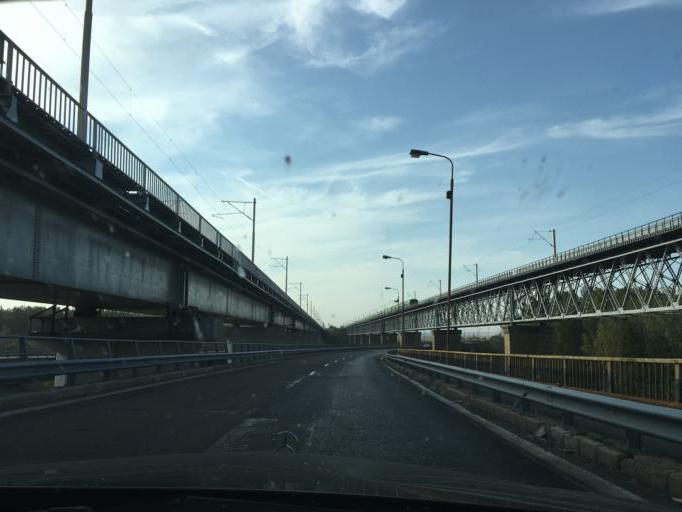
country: RO
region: Constanta
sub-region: Oras Cernavoda
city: Cernavoda
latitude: 44.3422
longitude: 28.0084
